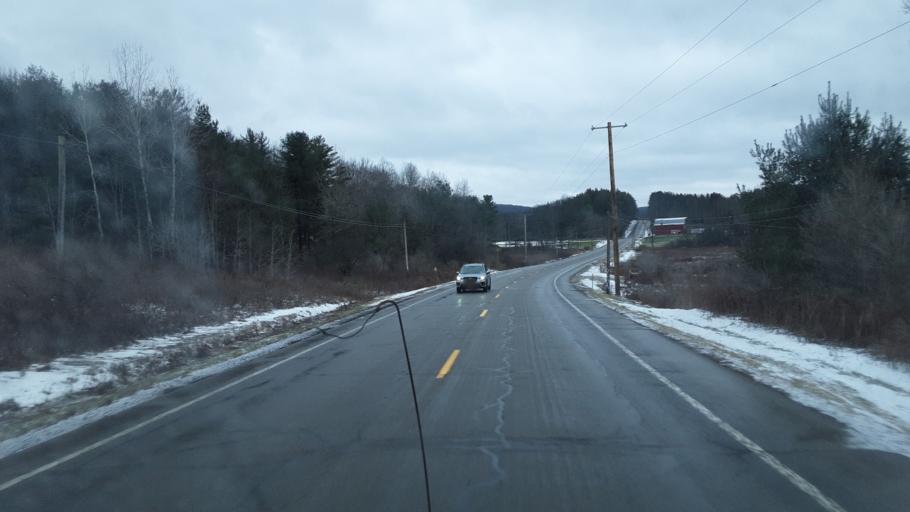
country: US
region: New York
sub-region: Allegany County
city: Houghton
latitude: 42.3168
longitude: -78.1273
